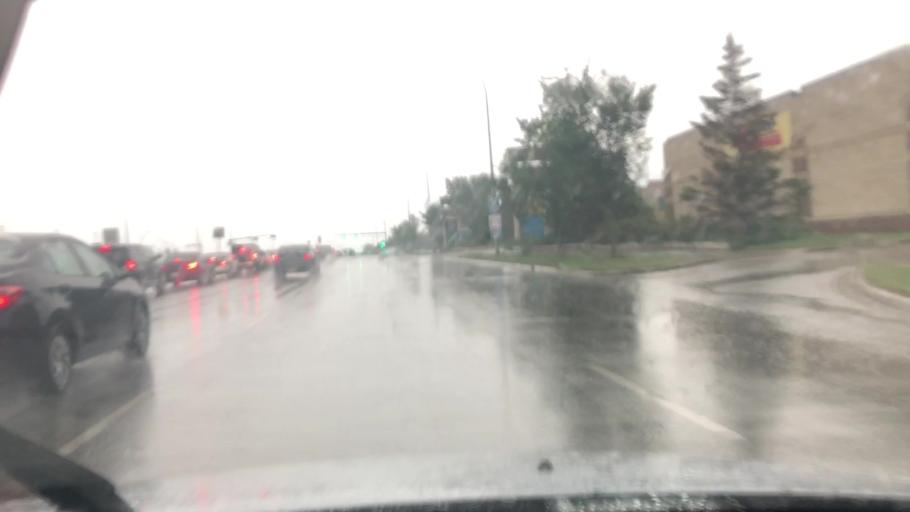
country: CA
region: Alberta
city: St. Albert
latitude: 53.5993
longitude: -113.5723
